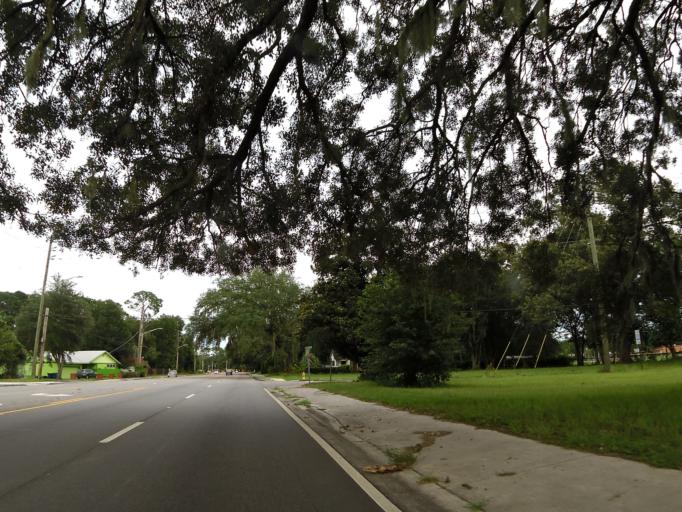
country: US
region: Florida
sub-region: Duval County
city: Jacksonville
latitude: 30.3848
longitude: -81.7097
